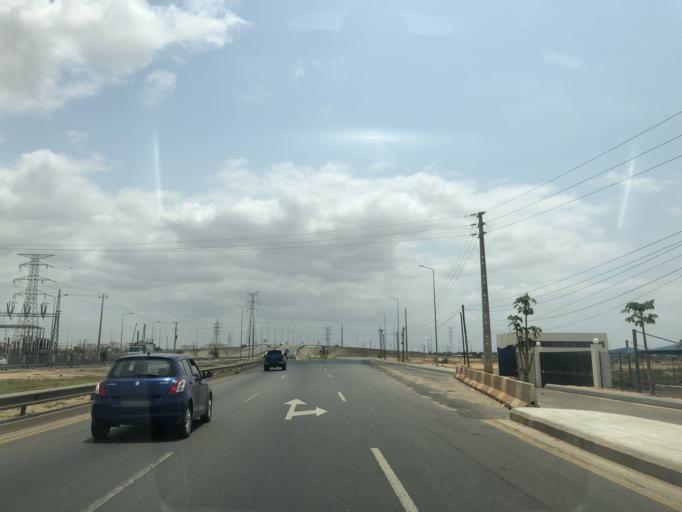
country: AO
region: Luanda
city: Luanda
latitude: -8.9693
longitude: 13.2548
